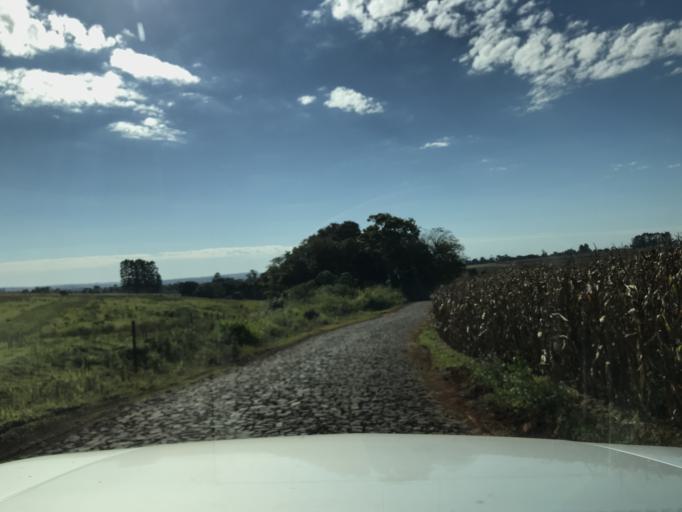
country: BR
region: Parana
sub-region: Palotina
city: Palotina
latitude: -24.2122
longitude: -53.7700
